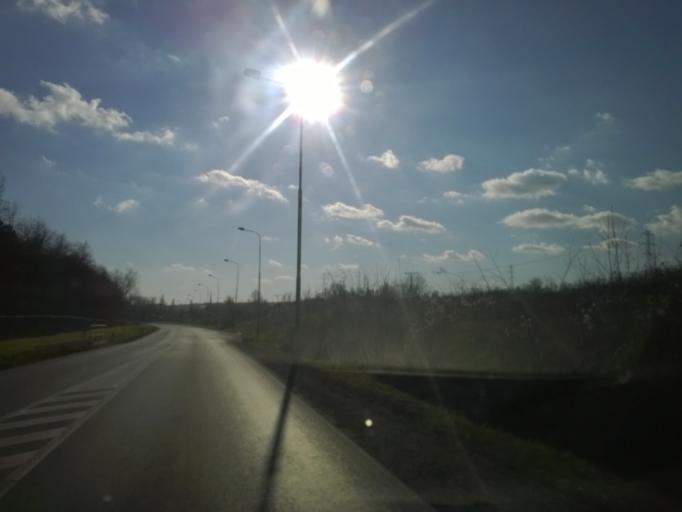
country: RS
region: Central Serbia
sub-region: Podunavski Okrug
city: Smederevo
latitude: 44.6082
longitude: 20.9608
